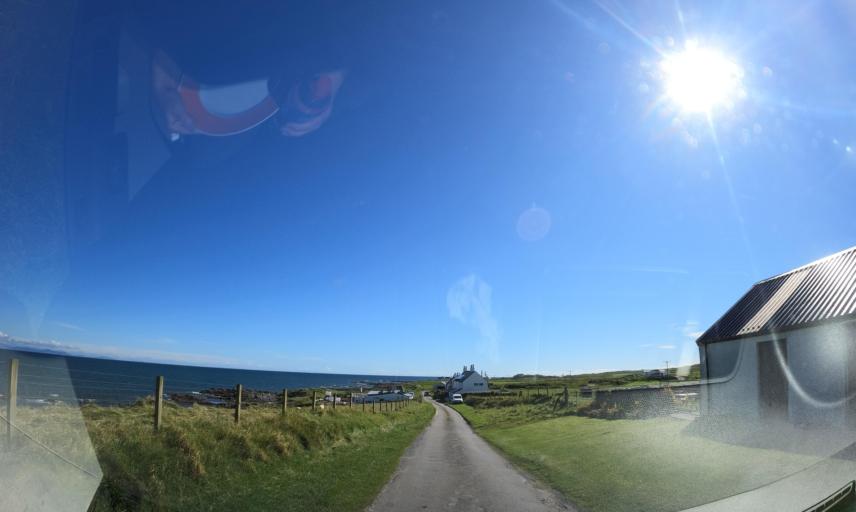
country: GB
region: Scotland
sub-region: Eilean Siar
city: Barra
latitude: 56.4656
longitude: -6.8961
